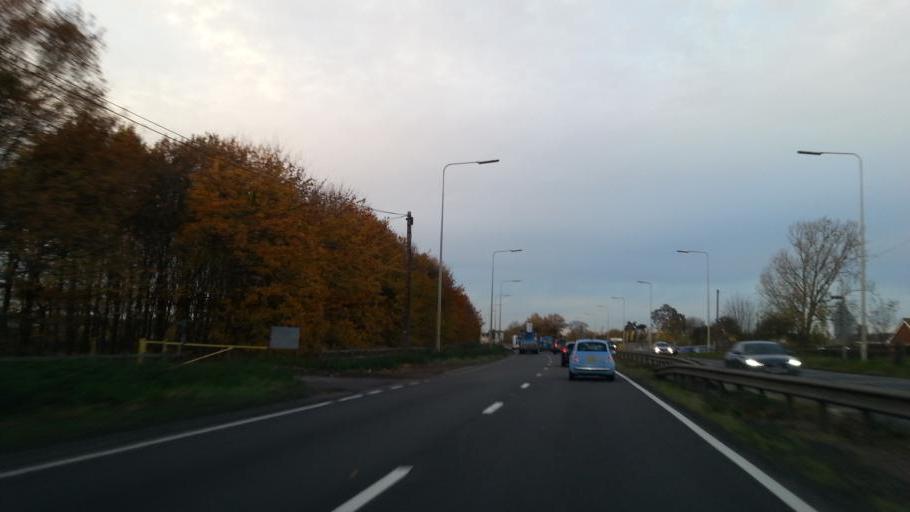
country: GB
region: England
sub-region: Central Bedfordshire
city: Biggleswade
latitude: 52.0956
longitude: -0.2748
